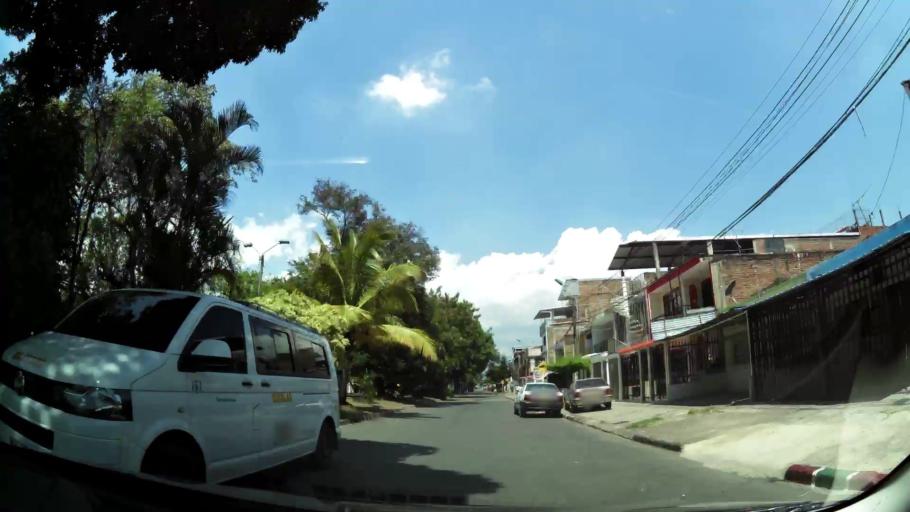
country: CO
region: Valle del Cauca
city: Cali
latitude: 3.4346
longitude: -76.4967
